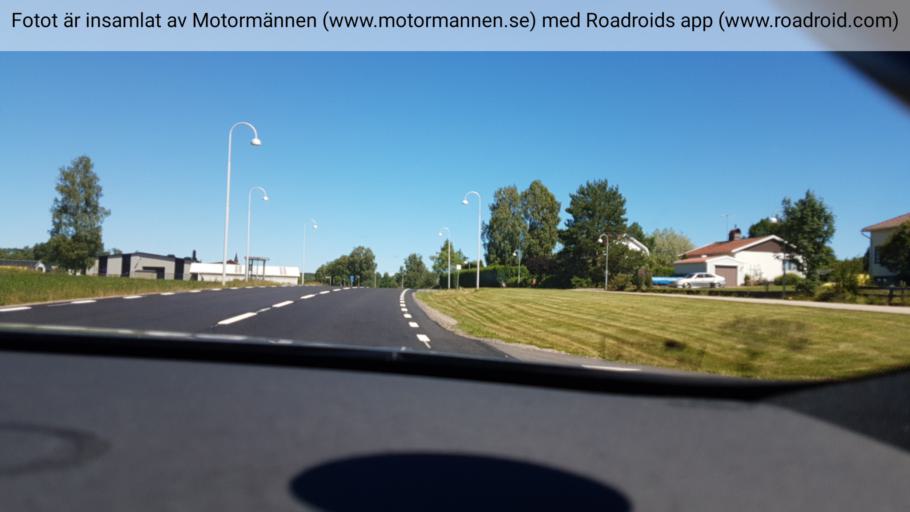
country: SE
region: Vaestra Goetaland
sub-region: Ulricehamns Kommun
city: Ulricehamn
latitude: 57.9201
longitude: 13.4882
